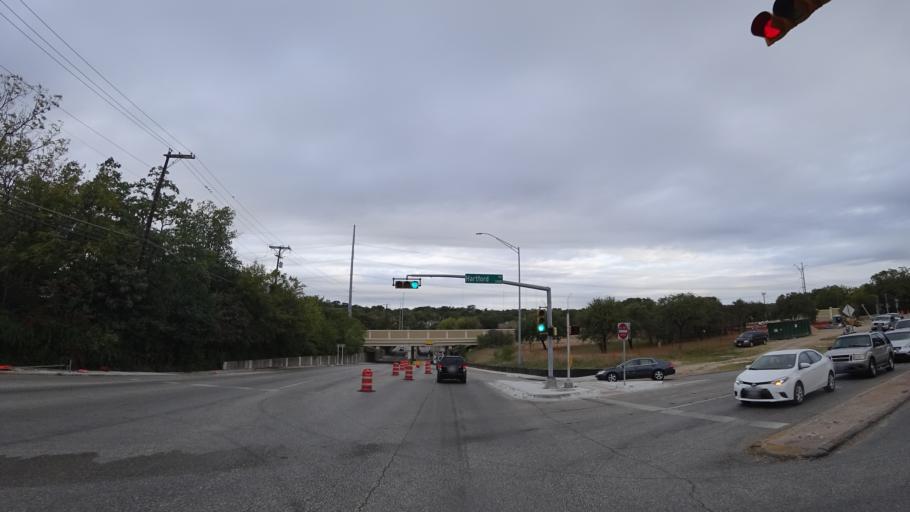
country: US
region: Texas
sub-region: Travis County
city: Austin
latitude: 30.2916
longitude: -97.7588
